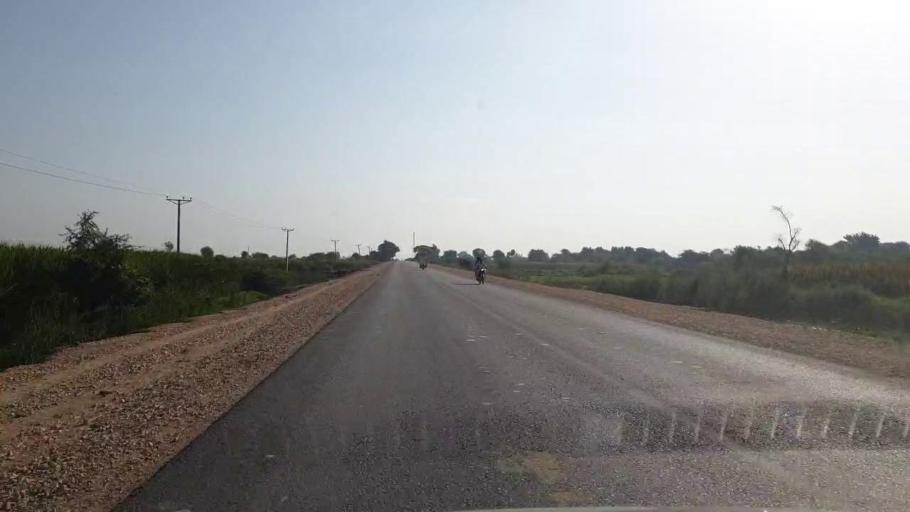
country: PK
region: Sindh
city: Badin
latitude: 24.6587
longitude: 68.9401
